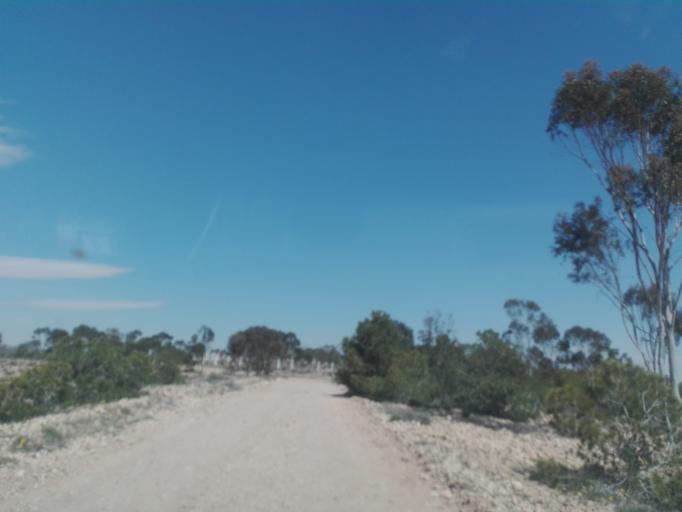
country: TN
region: Safaqis
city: Sfax
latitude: 34.7018
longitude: 10.5290
